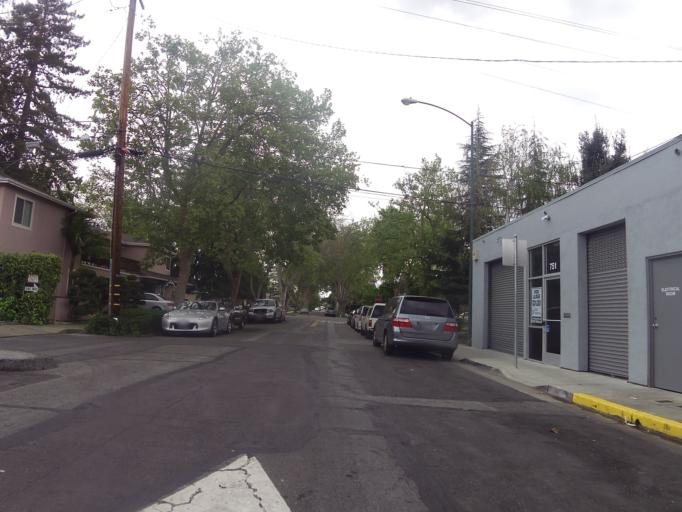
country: US
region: California
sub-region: Santa Clara County
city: Mountain View
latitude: 37.3863
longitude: -122.0833
